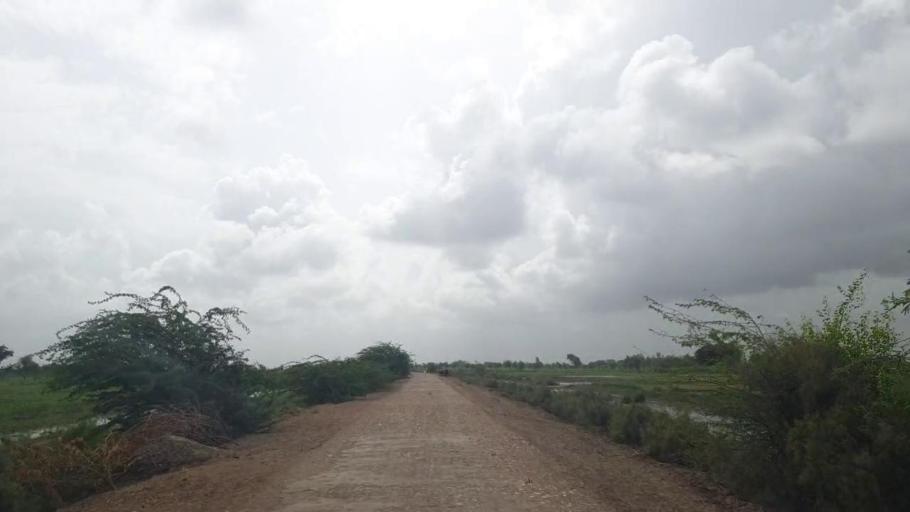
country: PK
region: Sindh
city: Tando Bago
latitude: 24.8270
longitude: 69.0806
